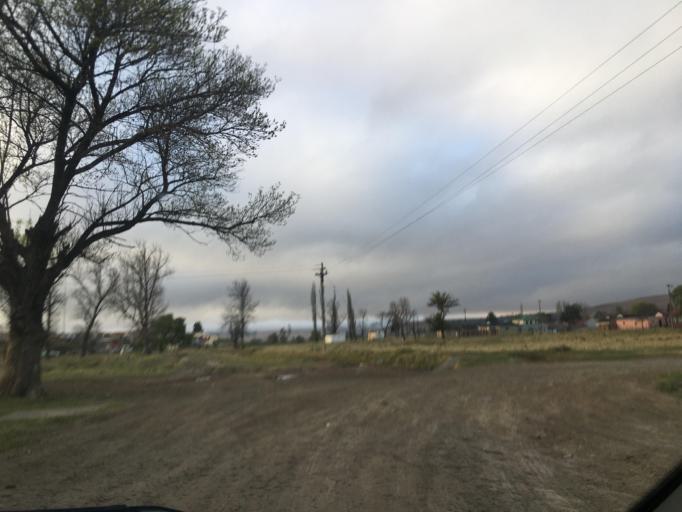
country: ZA
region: Eastern Cape
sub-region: Chris Hani District Municipality
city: Elliot
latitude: -31.3338
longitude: 27.8532
